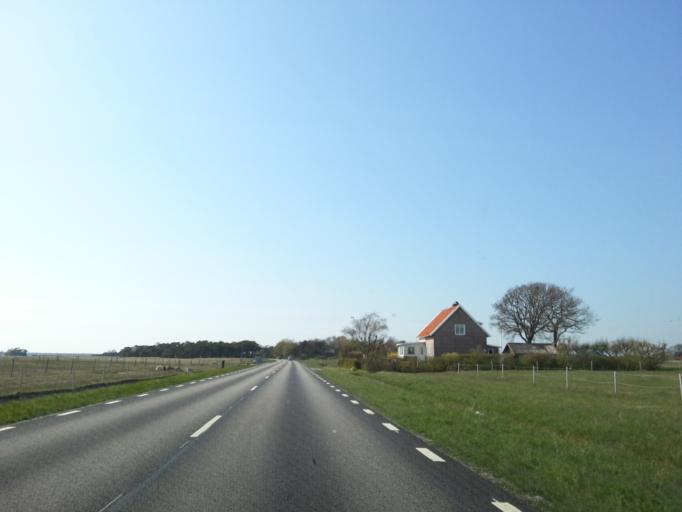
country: SE
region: Skane
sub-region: Trelleborgs Kommun
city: Skare
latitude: 55.3914
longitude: 13.0070
